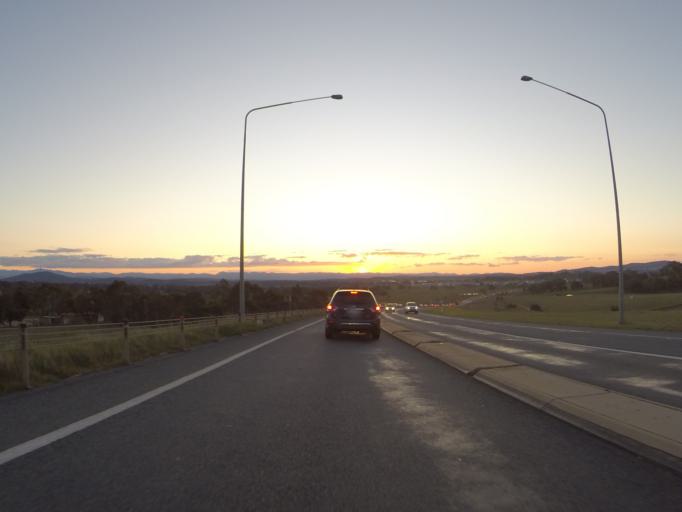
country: AU
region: Australian Capital Territory
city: Kaleen
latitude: -35.2132
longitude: 149.1814
